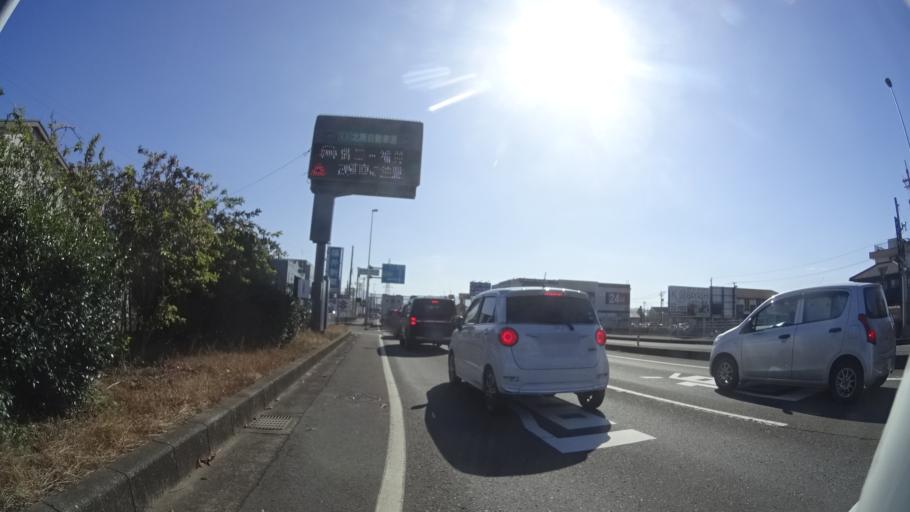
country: JP
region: Fukui
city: Sabae
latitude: 35.9508
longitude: 136.1924
